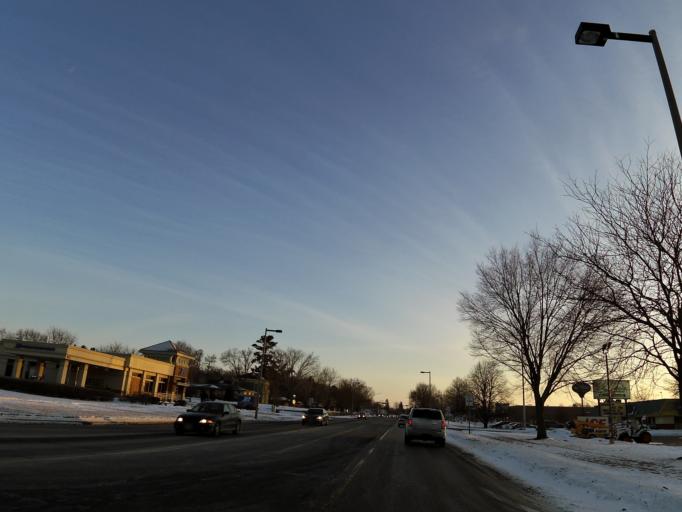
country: US
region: Wisconsin
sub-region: Pierce County
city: River Falls
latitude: 44.8721
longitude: -92.6218
